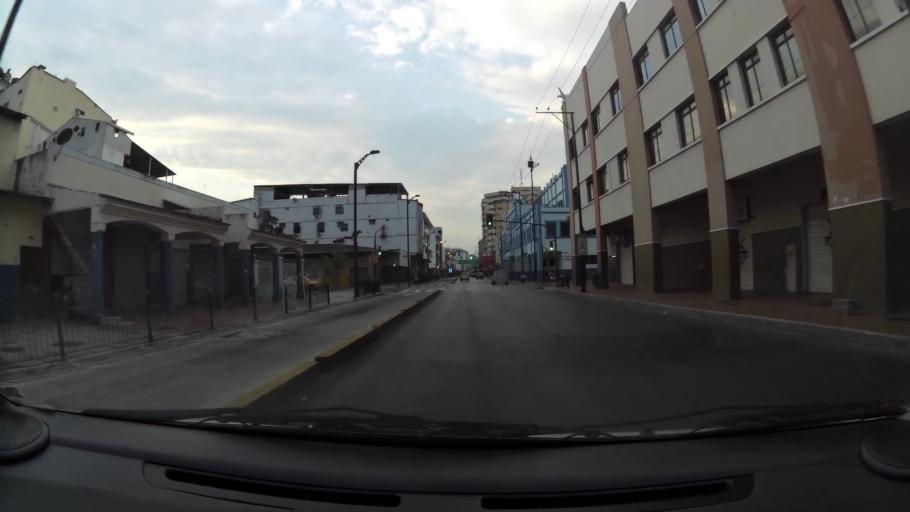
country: EC
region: Guayas
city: Guayaquil
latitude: -2.2050
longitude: -79.8847
